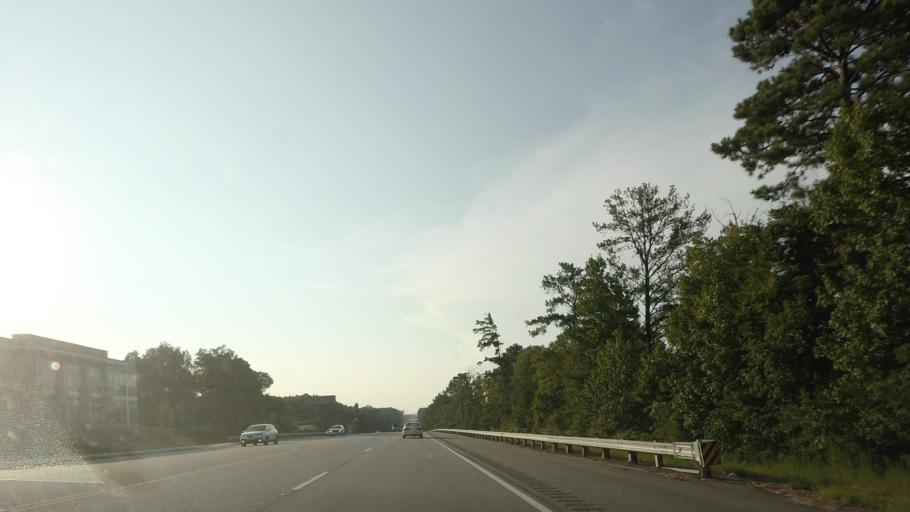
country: US
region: Georgia
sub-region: Bibb County
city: Macon
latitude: 32.9065
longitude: -83.6925
